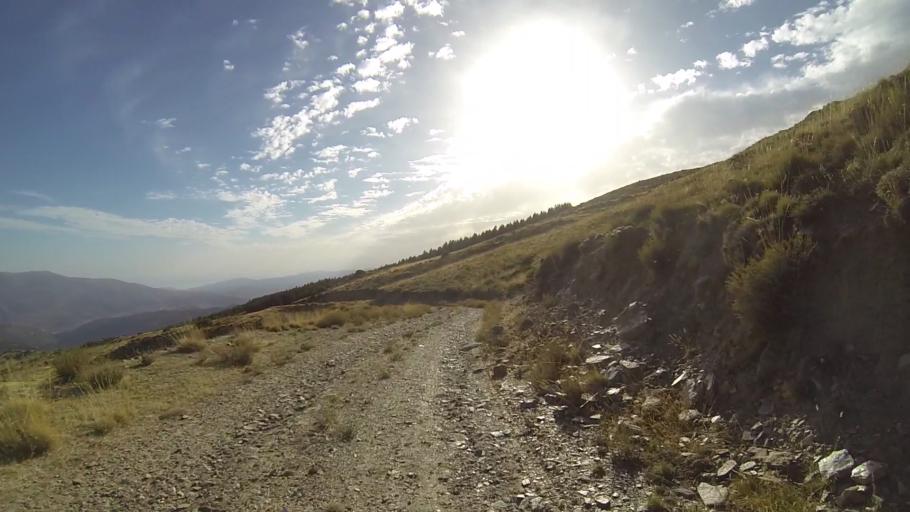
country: ES
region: Andalusia
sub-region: Provincia de Almeria
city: Laujar de Andarax
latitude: 37.0739
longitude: -2.8886
